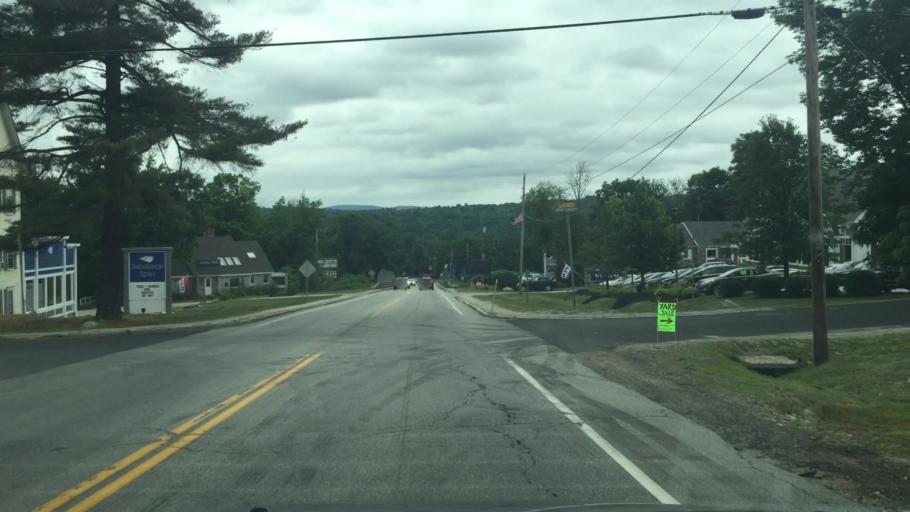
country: US
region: New Hampshire
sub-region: Belknap County
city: Meredith
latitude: 43.6494
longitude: -71.4989
